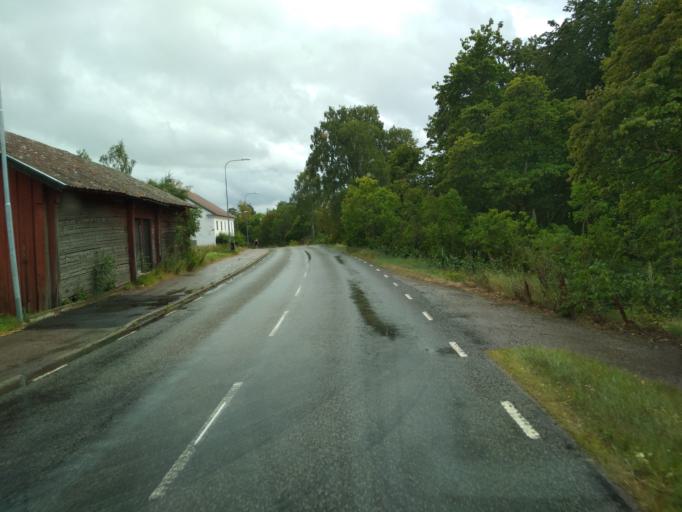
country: SE
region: Vaestmanland
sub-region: Surahammars Kommun
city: Ramnas
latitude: 59.7807
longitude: 16.1871
